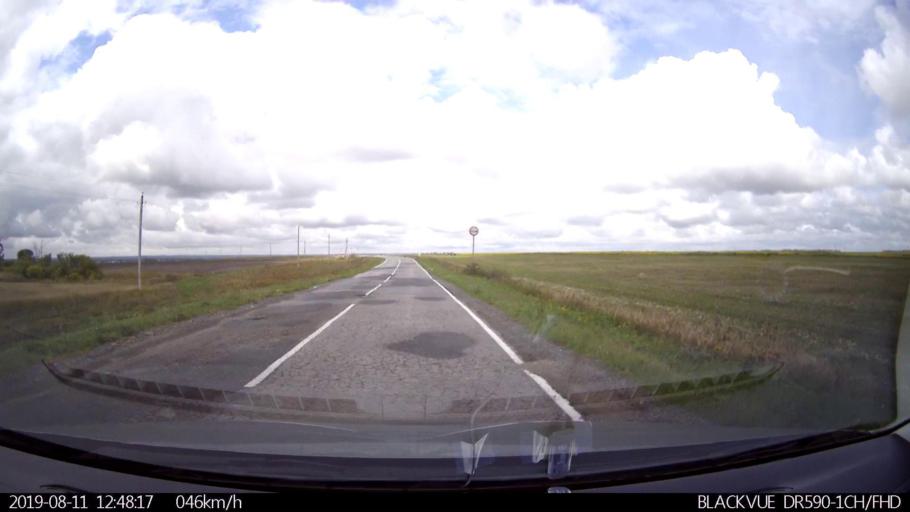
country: RU
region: Ulyanovsk
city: Ignatovka
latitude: 53.8732
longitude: 47.7006
